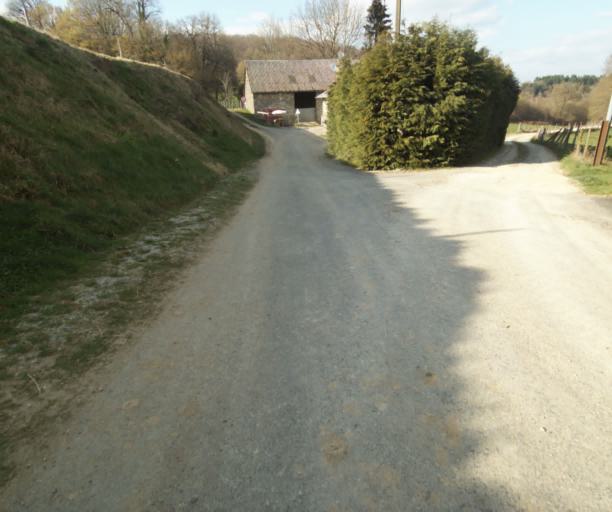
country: FR
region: Limousin
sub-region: Departement de la Correze
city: Saint-Mexant
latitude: 45.3452
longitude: 1.6098
